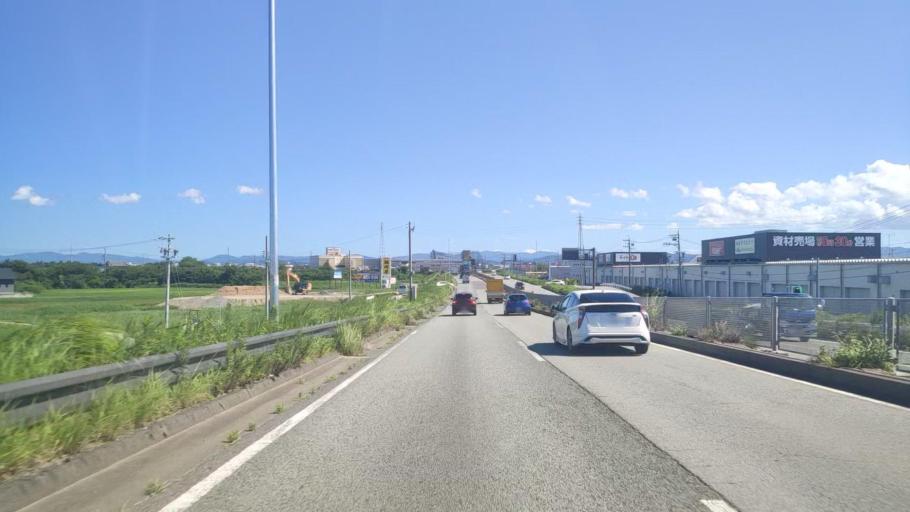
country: JP
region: Mie
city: Hisai-motomachi
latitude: 34.6105
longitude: 136.5188
